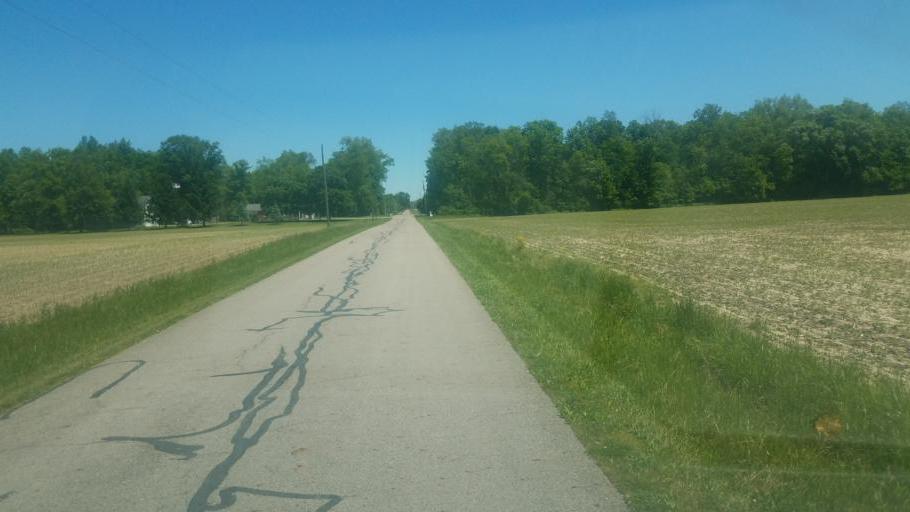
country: US
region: Ohio
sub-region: Darke County
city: Versailles
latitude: 40.2265
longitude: -84.3926
